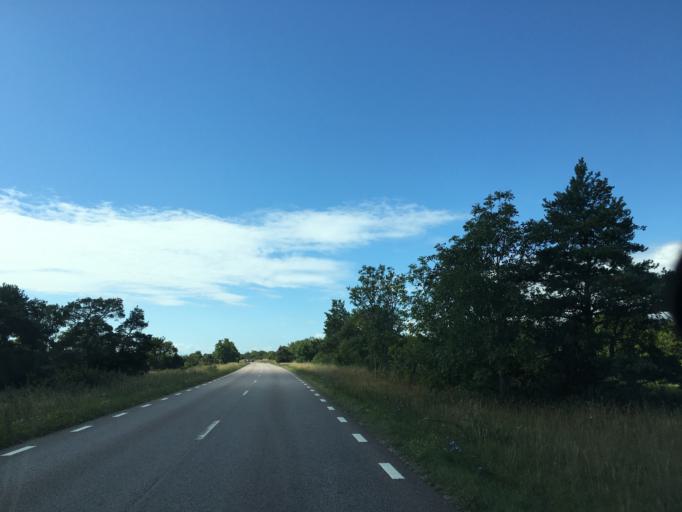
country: SE
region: Kalmar
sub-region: Morbylanga Kommun
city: Moerbylanga
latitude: 56.5624
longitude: 16.4501
